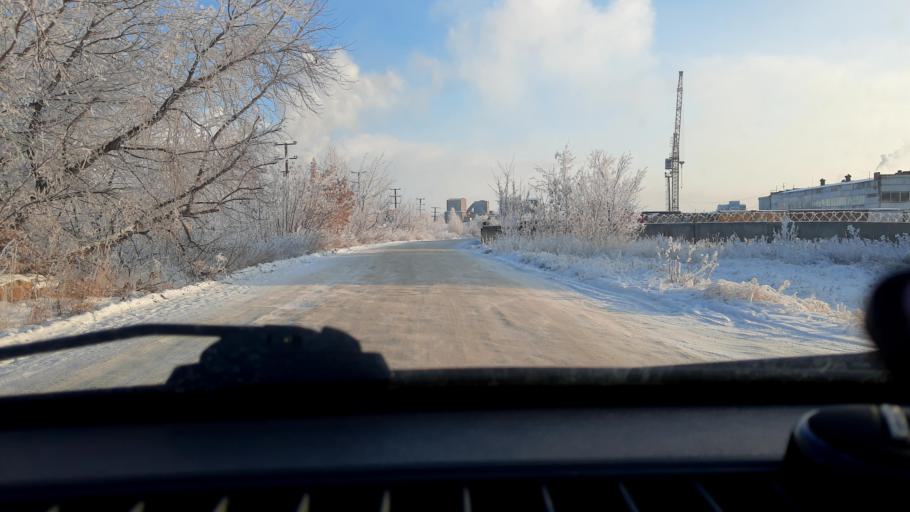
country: RU
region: Bashkortostan
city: Iglino
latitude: 54.7710
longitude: 56.2430
